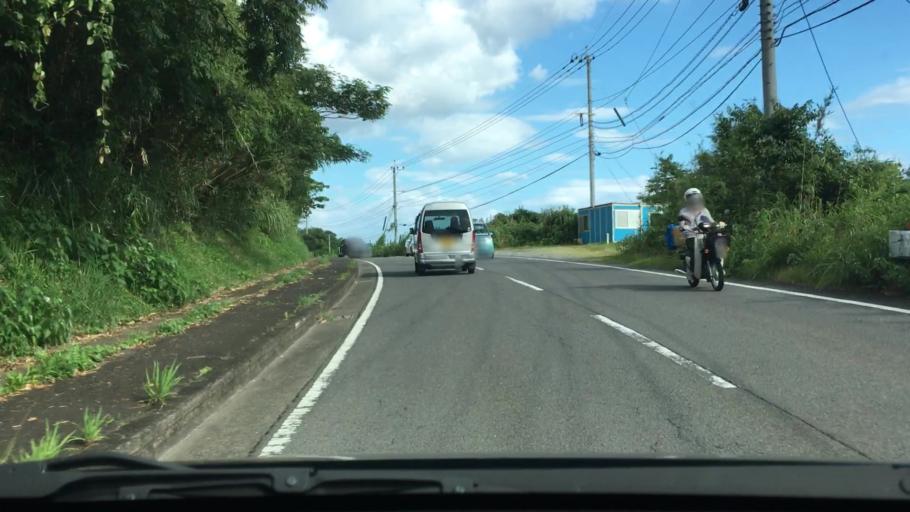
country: JP
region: Nagasaki
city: Togitsu
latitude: 32.8203
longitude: 129.7355
